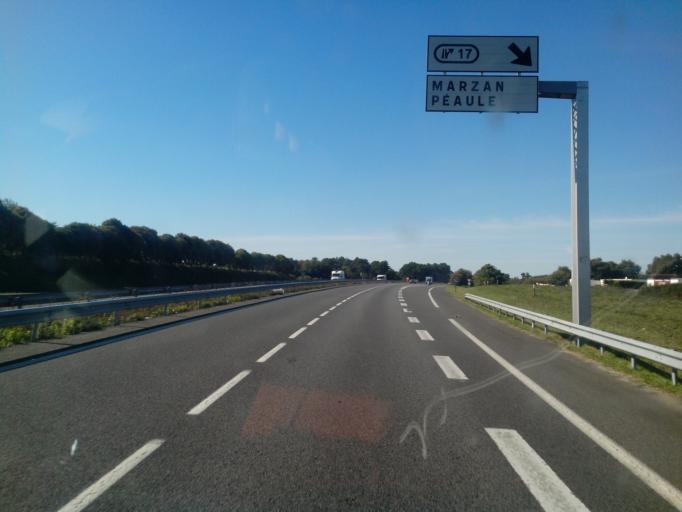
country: FR
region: Brittany
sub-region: Departement du Morbihan
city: Marzan
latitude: 47.5298
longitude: -2.3258
